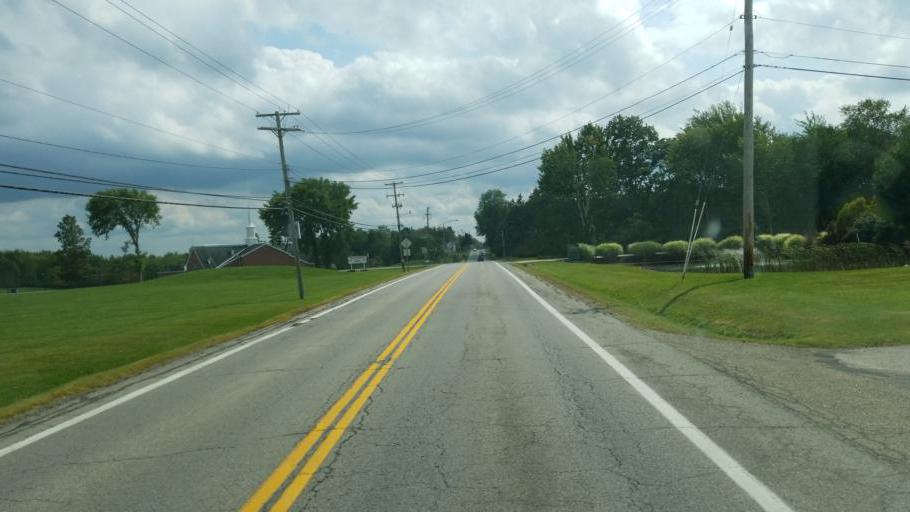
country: US
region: Ohio
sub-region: Geauga County
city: Burton
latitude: 41.5048
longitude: -81.1936
